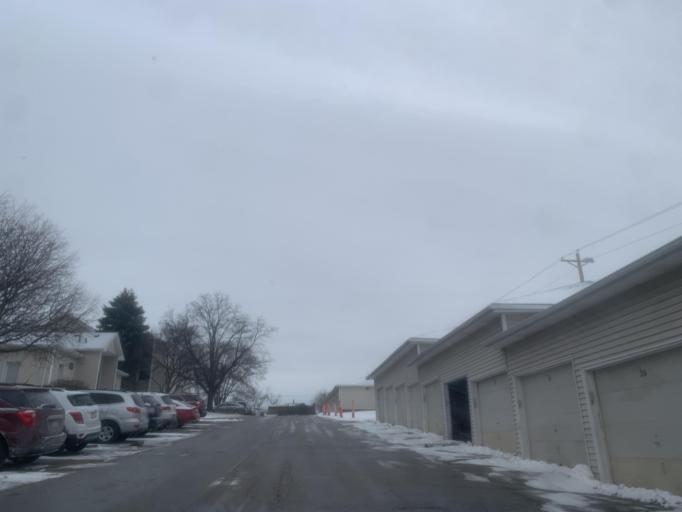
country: US
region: Nebraska
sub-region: Douglas County
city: Ralston
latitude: 41.2722
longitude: -96.0809
